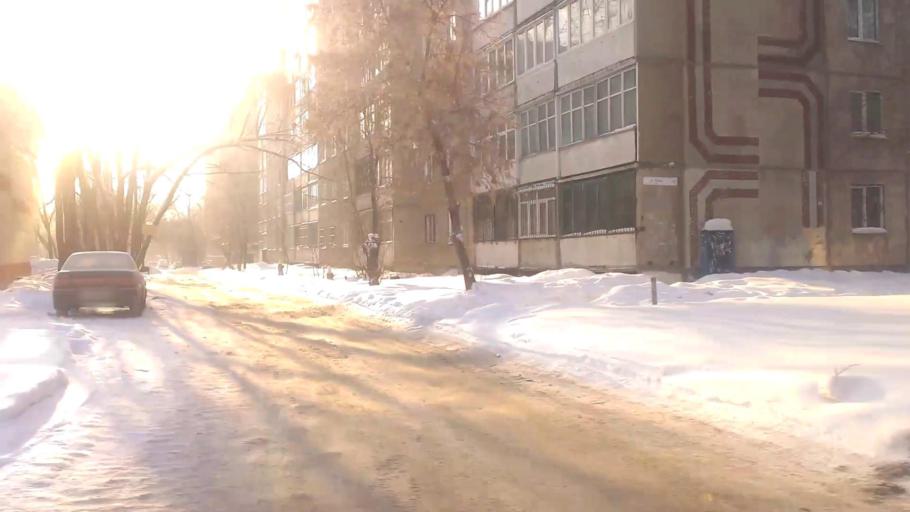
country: RU
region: Altai Krai
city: Novosilikatnyy
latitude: 53.3745
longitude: 83.6656
